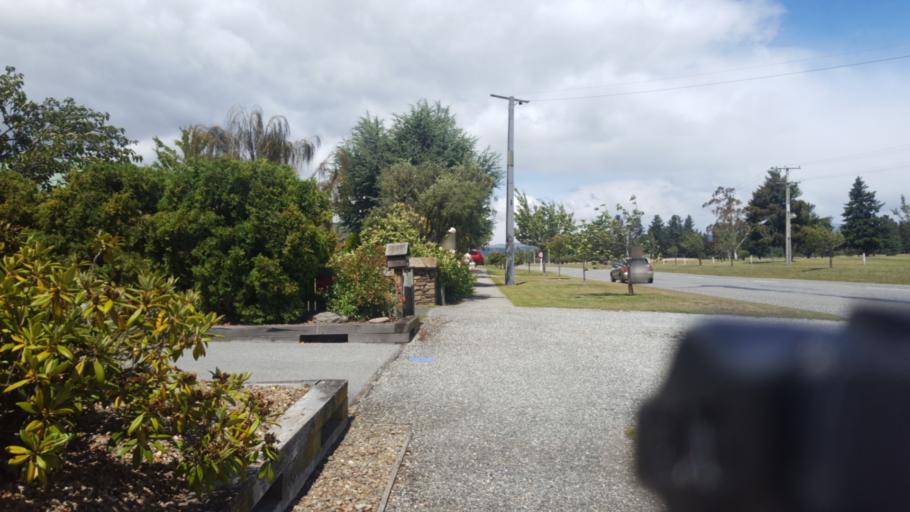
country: NZ
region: Otago
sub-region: Queenstown-Lakes District
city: Wanaka
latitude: -45.1940
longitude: 169.3261
